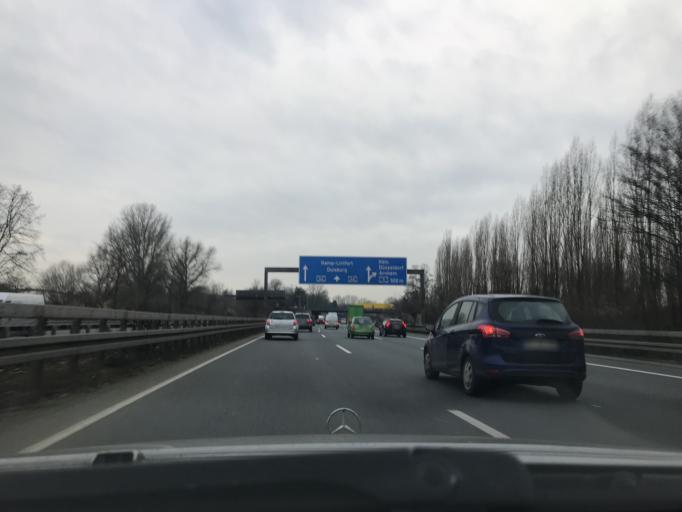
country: DE
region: North Rhine-Westphalia
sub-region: Regierungsbezirk Dusseldorf
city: Oberhausen
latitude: 51.4867
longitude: 6.8304
